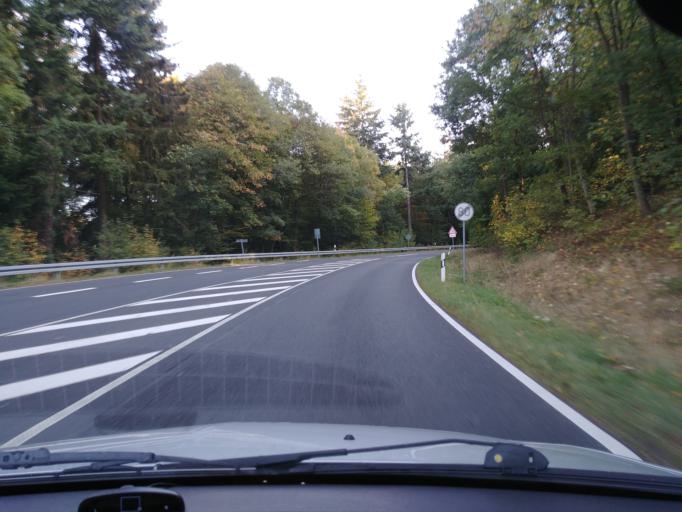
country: DE
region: Hesse
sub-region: Regierungsbezirk Darmstadt
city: Waldems
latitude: 50.2824
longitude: 8.3672
